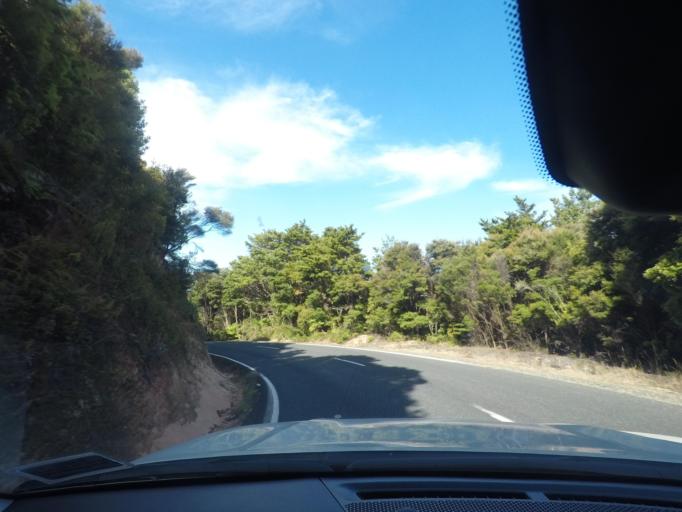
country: NZ
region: Northland
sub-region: Whangarei
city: Ngunguru
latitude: -35.6664
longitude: 174.4732
